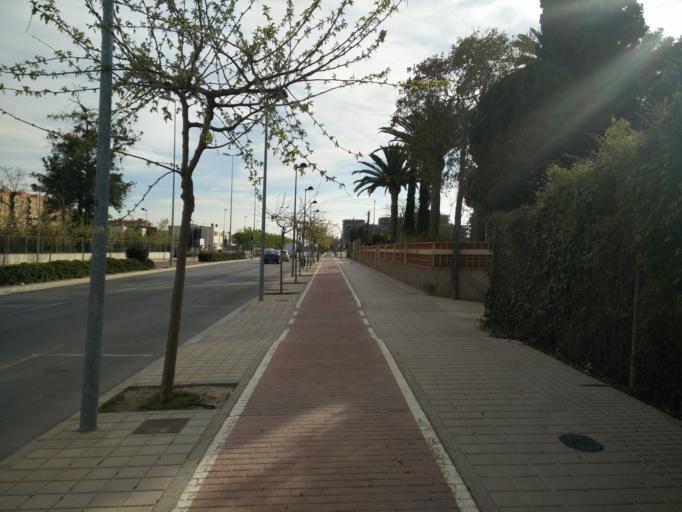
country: ES
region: Valencia
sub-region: Provincia de Castello
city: Castello de la Plana
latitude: 39.9803
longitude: -0.0542
